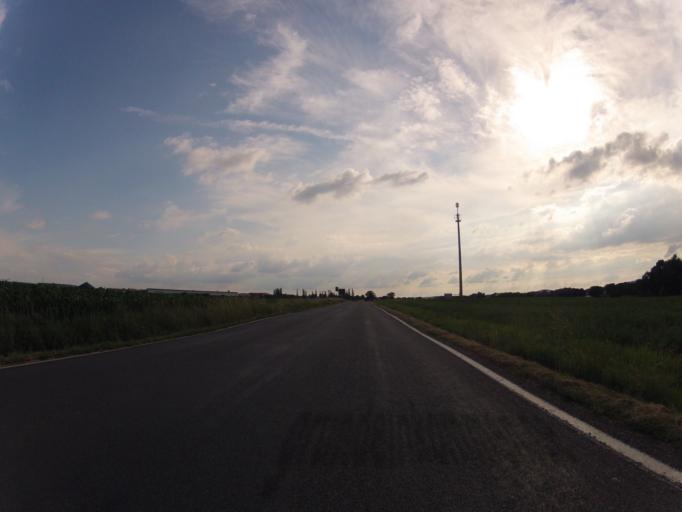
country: DE
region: Saxony
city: Falkenhain
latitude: 51.4074
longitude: 12.8836
